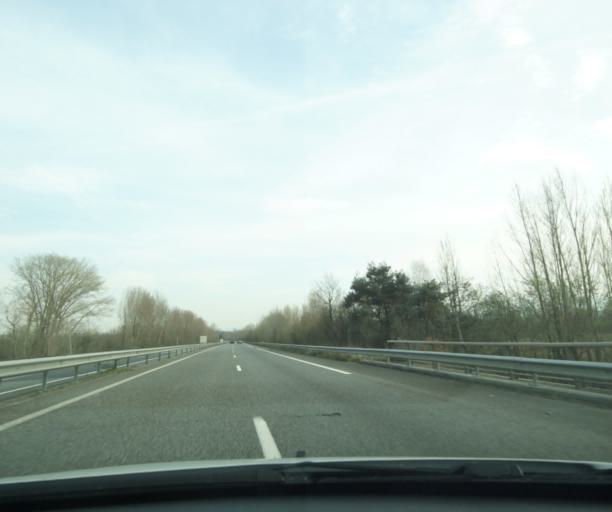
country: FR
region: Midi-Pyrenees
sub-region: Departement des Hautes-Pyrenees
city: Juillan
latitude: 43.2142
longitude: 0.0314
